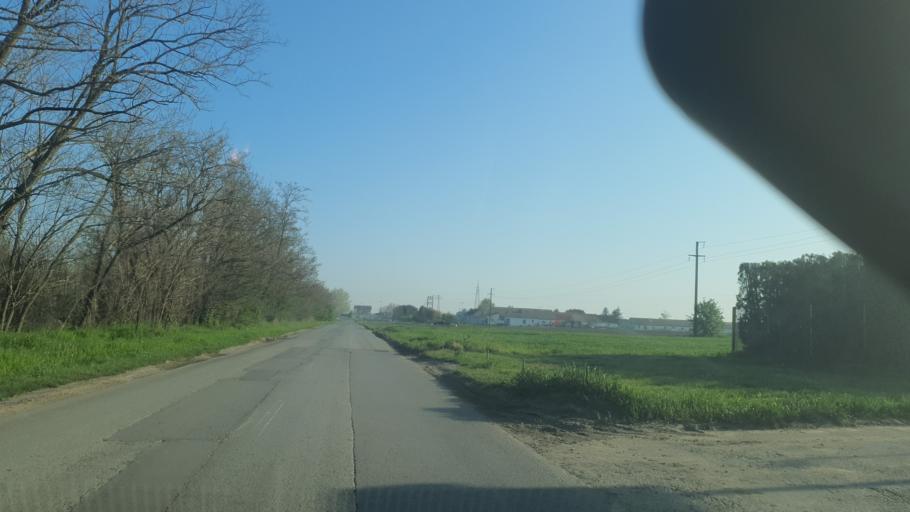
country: RS
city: Rumenka
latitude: 45.2635
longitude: 19.7007
